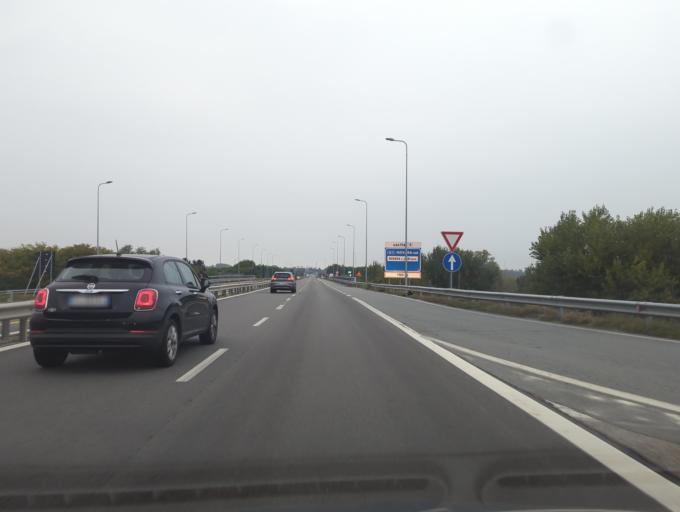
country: IT
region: Piedmont
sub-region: Provincia di Novara
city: Pernate
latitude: 45.4399
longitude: 8.6689
